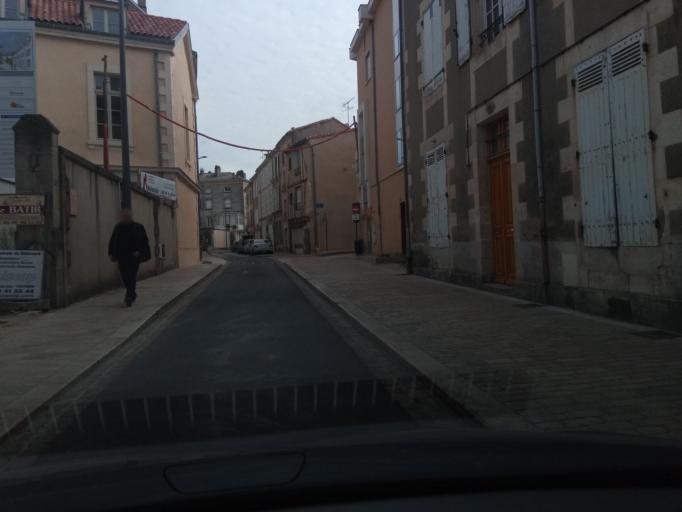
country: FR
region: Poitou-Charentes
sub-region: Departement de la Vienne
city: Poitiers
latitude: 46.5762
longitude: 0.3331
